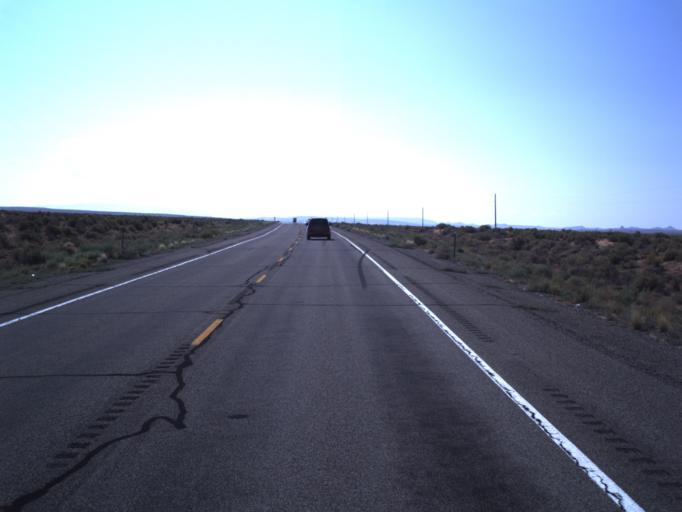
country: US
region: Utah
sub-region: San Juan County
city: Blanding
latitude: 37.2031
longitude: -109.6058
